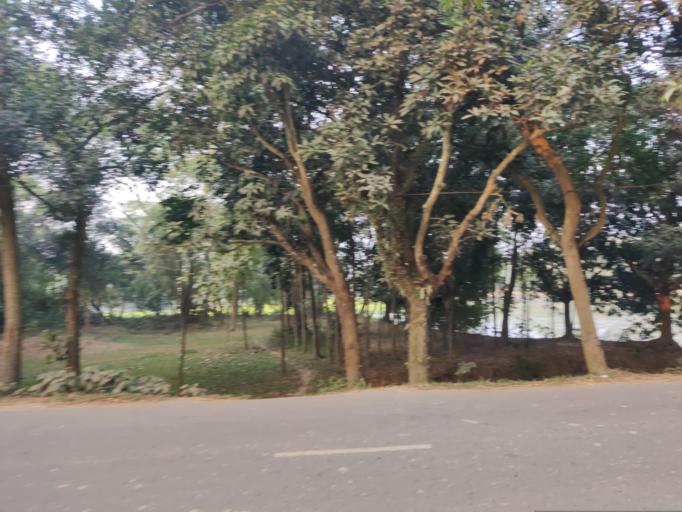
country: BD
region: Dhaka
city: Bajitpur
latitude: 24.1580
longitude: 90.7616
